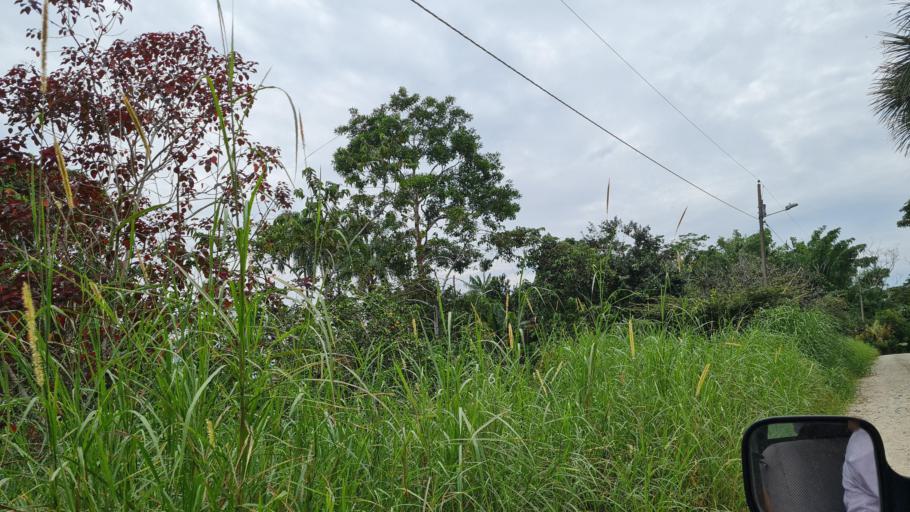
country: EC
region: Napo
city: Tena
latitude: -0.9990
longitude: -77.7560
